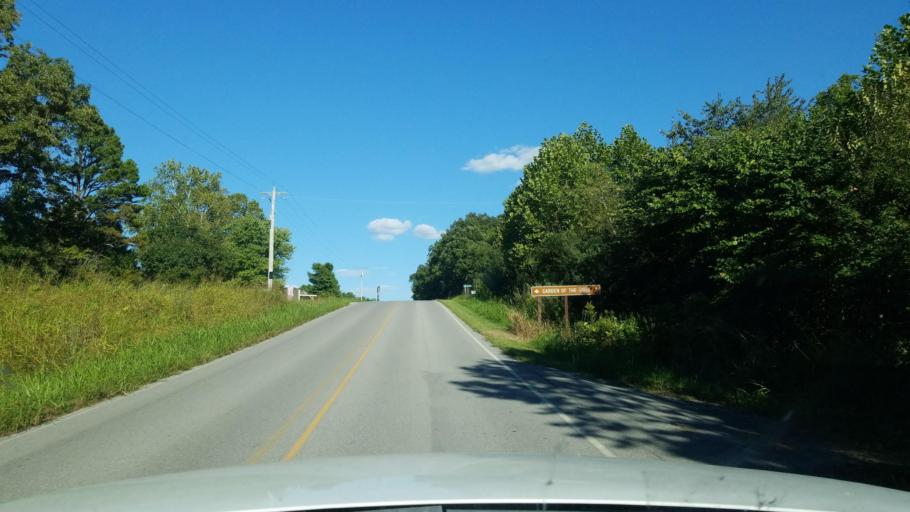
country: US
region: Illinois
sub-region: Hardin County
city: Elizabethtown
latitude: 37.5815
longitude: -88.3666
